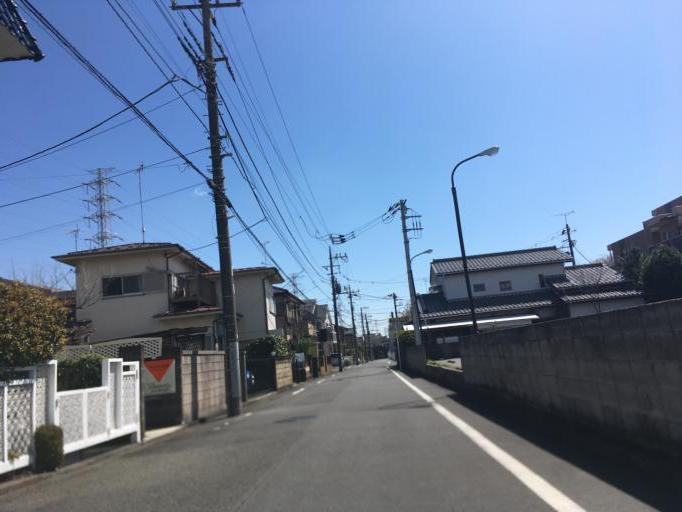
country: JP
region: Tokyo
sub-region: Machida-shi
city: Machida
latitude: 35.5708
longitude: 139.3801
